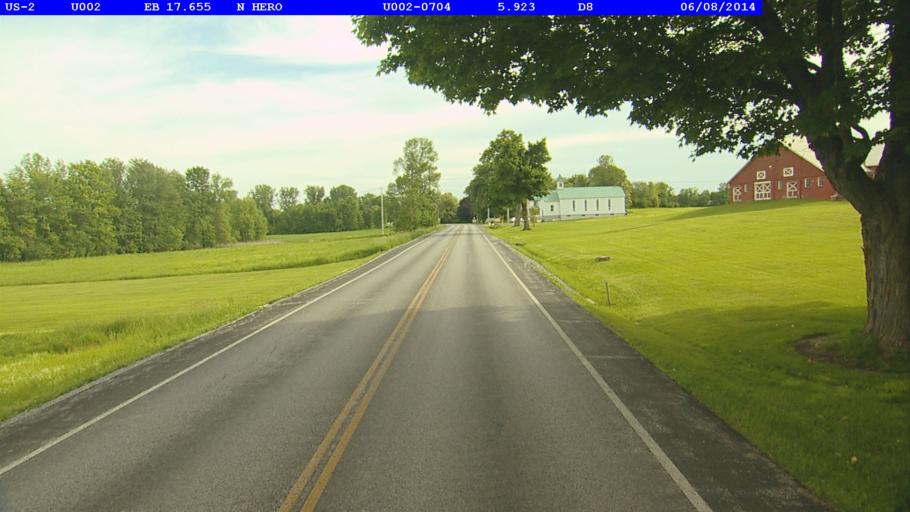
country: US
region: Vermont
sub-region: Grand Isle County
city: North Hero
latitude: 44.8140
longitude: -73.2914
